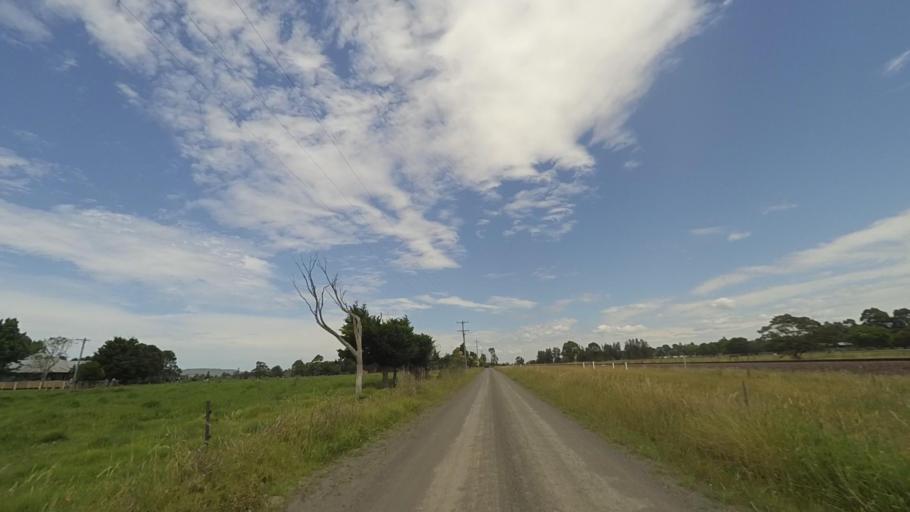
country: AU
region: New South Wales
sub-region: Shoalhaven Shire
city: Berry
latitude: -34.7919
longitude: 150.6784
